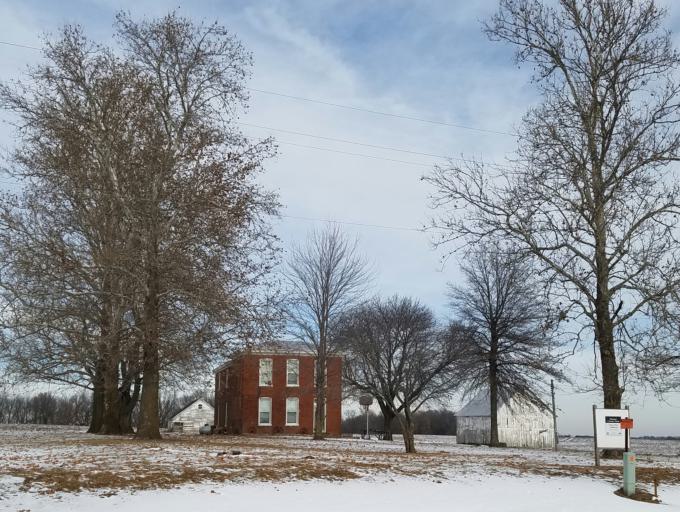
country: US
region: Missouri
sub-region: Lafayette County
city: Lexington
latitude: 39.1796
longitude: -93.7934
